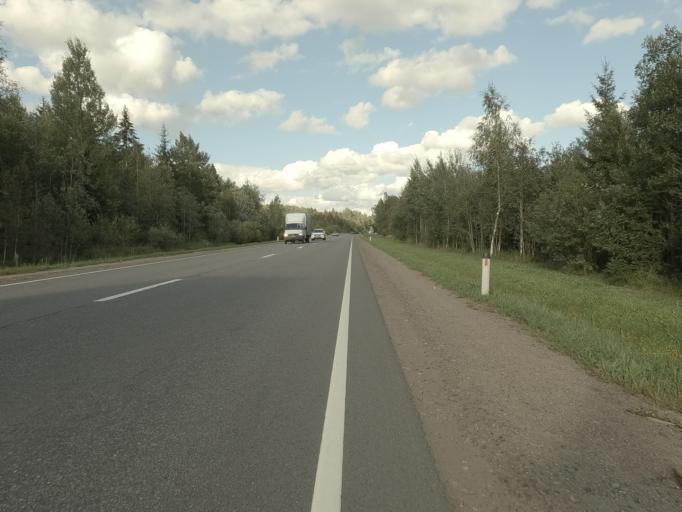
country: RU
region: Leningrad
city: Nikol'skoye
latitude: 59.6641
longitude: 30.8794
